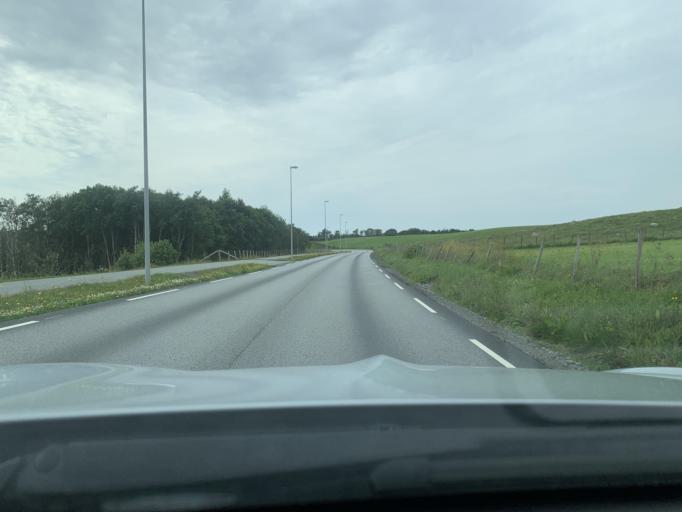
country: NO
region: Rogaland
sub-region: Time
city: Bryne
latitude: 58.7639
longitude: 5.7140
